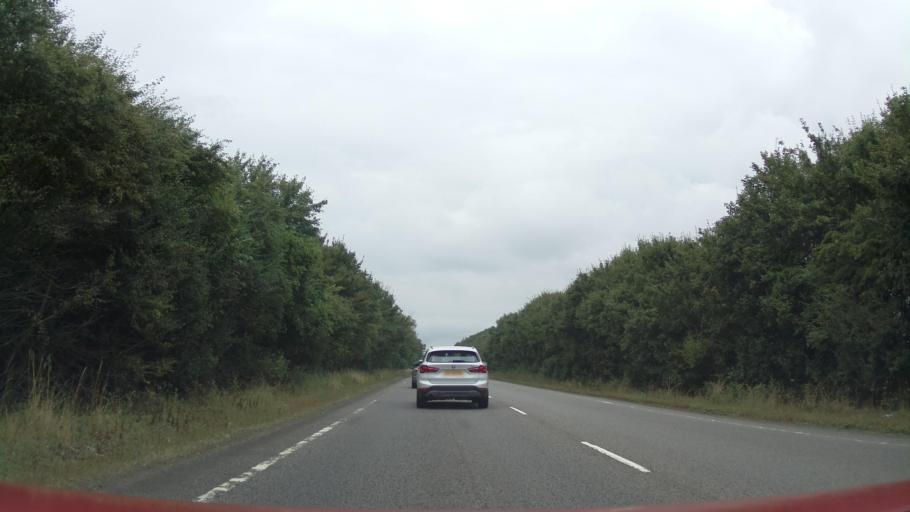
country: GB
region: England
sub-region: Nottinghamshire
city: South Collingham
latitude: 53.0910
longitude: -0.7647
